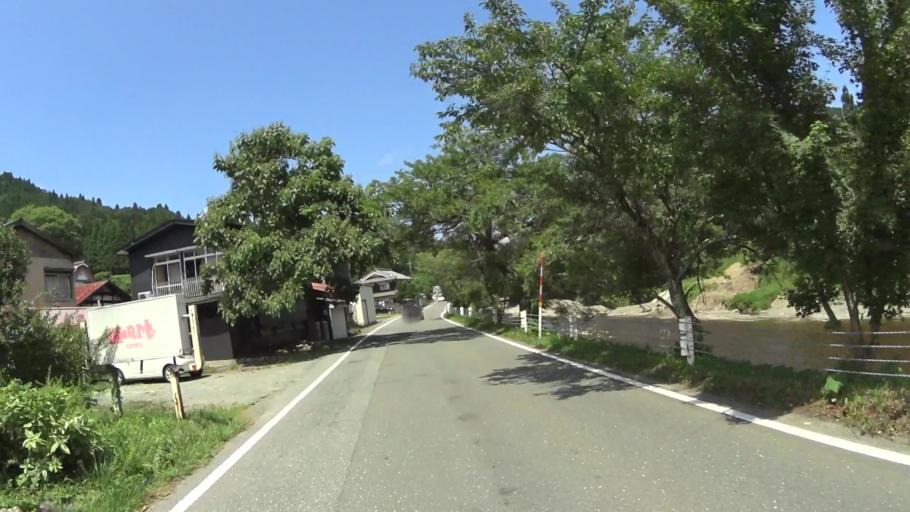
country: JP
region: Shiga Prefecture
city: Kitahama
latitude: 35.3572
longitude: 135.9187
